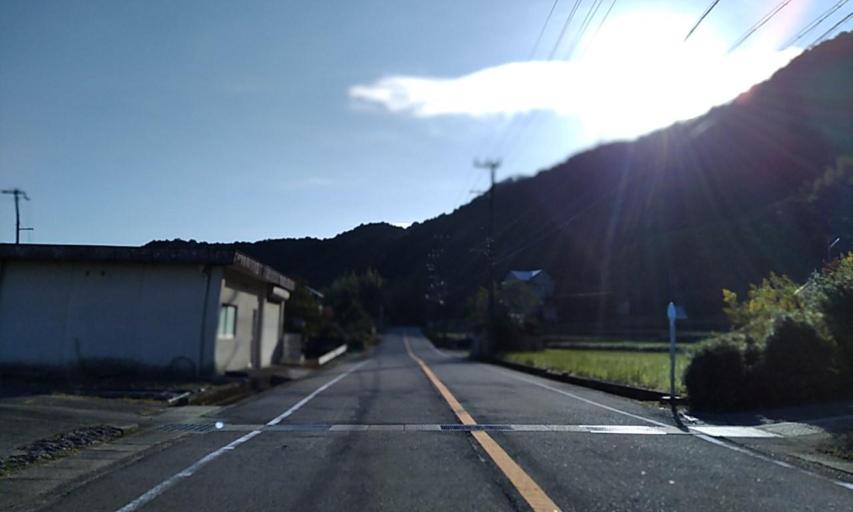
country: JP
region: Wakayama
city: Iwade
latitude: 34.1520
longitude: 135.3131
